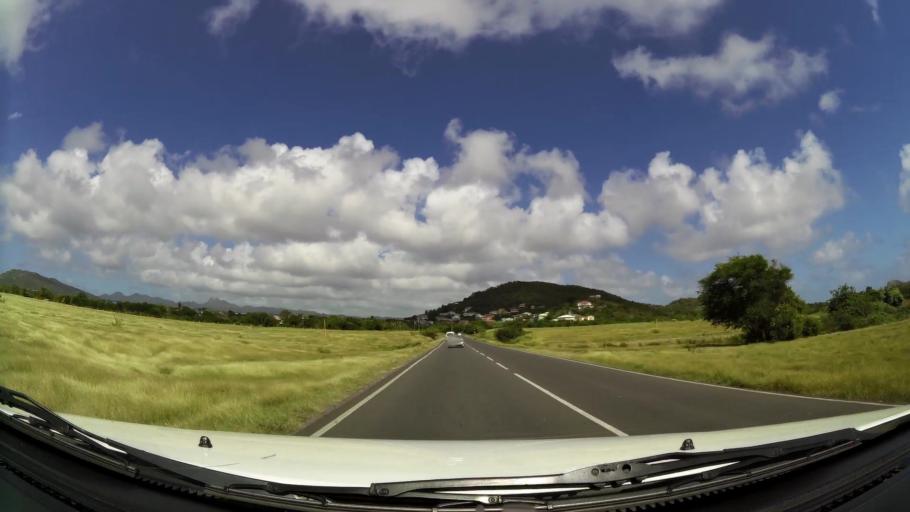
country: LC
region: Laborie Quarter
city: Laborie
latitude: 13.7329
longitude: -60.9699
